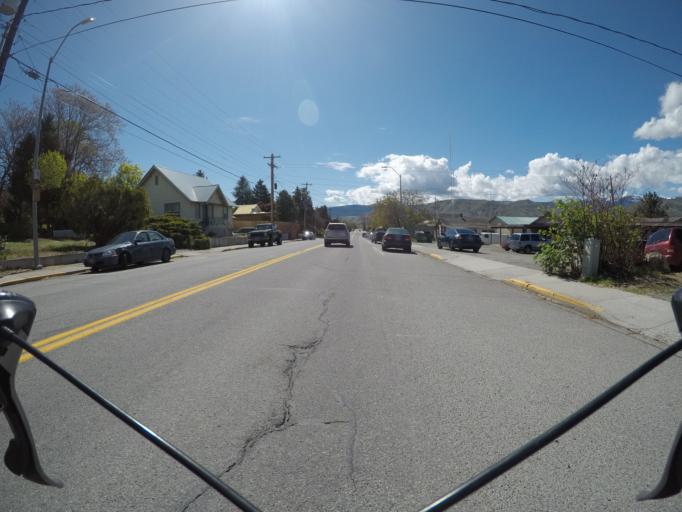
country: US
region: Washington
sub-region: Douglas County
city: East Wenatchee
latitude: 47.4183
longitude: -120.2921
